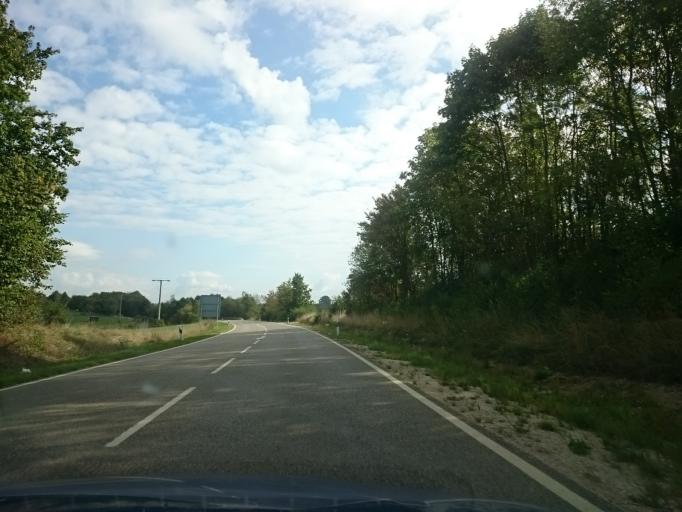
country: DE
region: Bavaria
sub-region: Regierungsbezirk Mittelfranken
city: Allersberg
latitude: 49.2346
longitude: 11.2108
